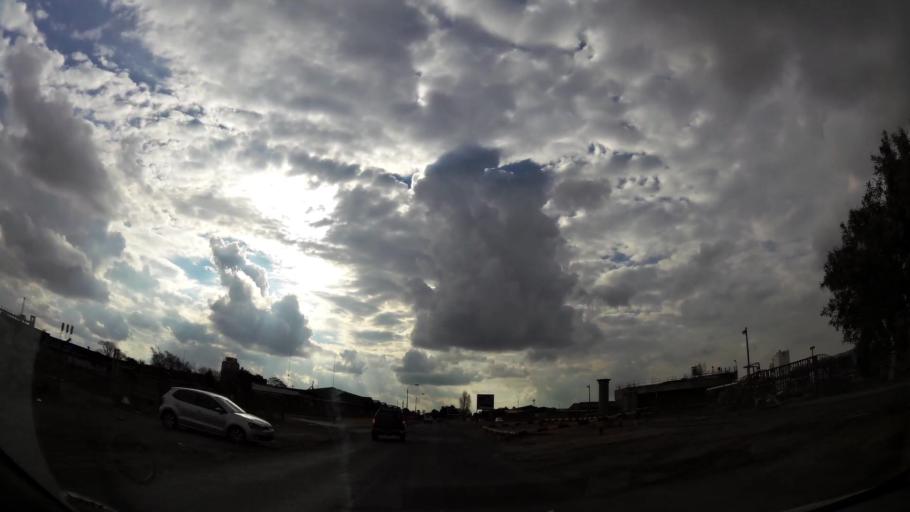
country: ZA
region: Orange Free State
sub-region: Fezile Dabi District Municipality
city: Sasolburg
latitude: -26.8245
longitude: 27.8366
